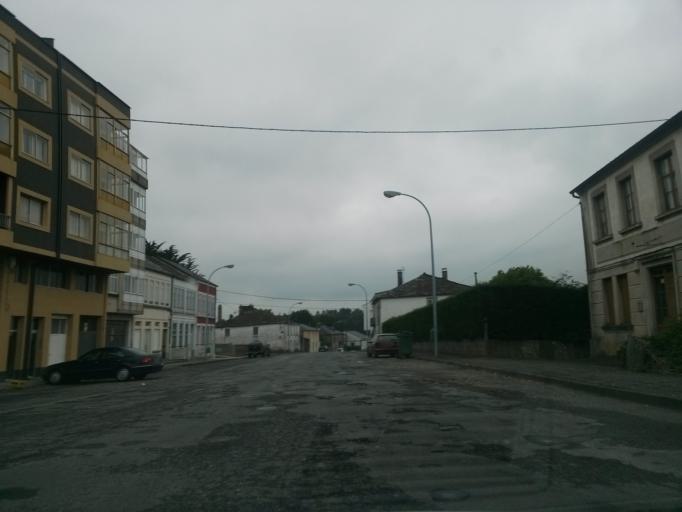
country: ES
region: Galicia
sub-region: Provincia de Lugo
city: Rabade
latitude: 43.1169
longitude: -7.6186
